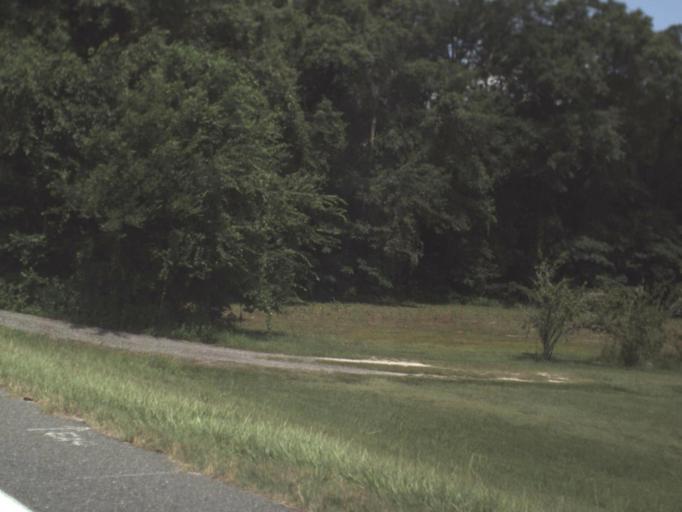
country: US
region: Florida
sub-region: Union County
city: Lake Butler
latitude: 29.9518
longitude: -82.4208
